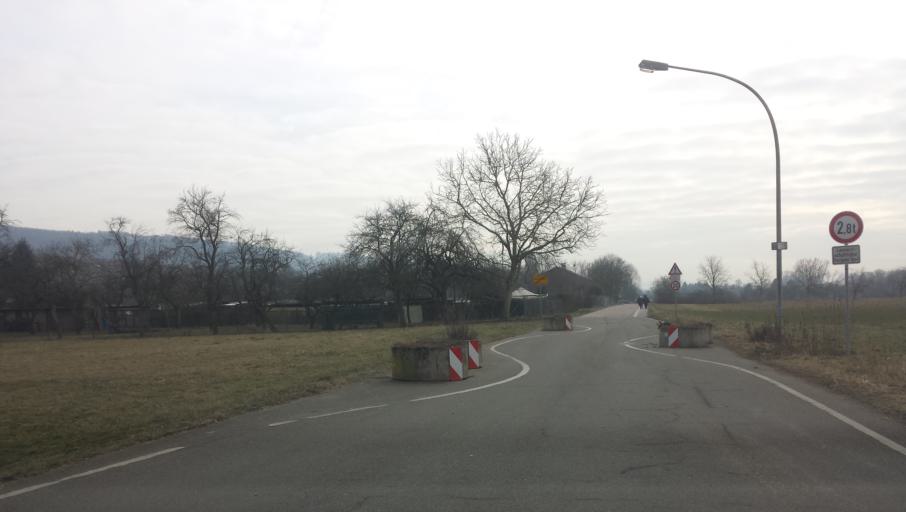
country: DE
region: Hesse
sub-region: Regierungsbezirk Darmstadt
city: Heppenheim an der Bergstrasse
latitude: 49.6315
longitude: 8.6361
